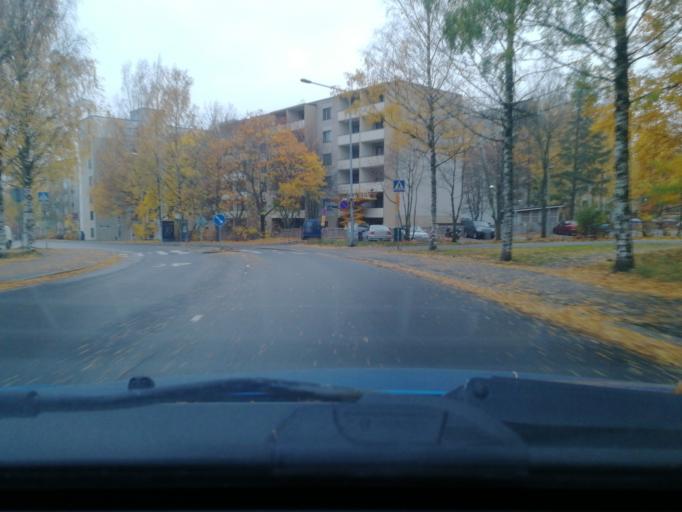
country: FI
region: Pirkanmaa
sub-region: Tampere
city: Tampere
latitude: 61.4421
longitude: 23.8532
